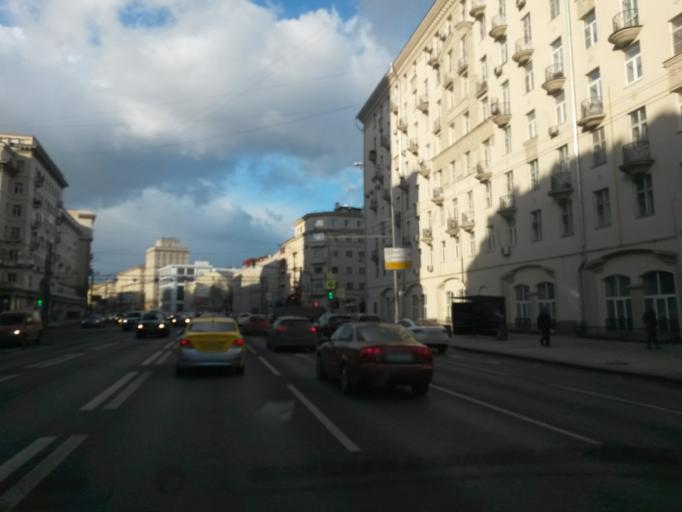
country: RU
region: Moscow
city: Mar'ina Roshcha
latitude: 55.7831
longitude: 37.6344
